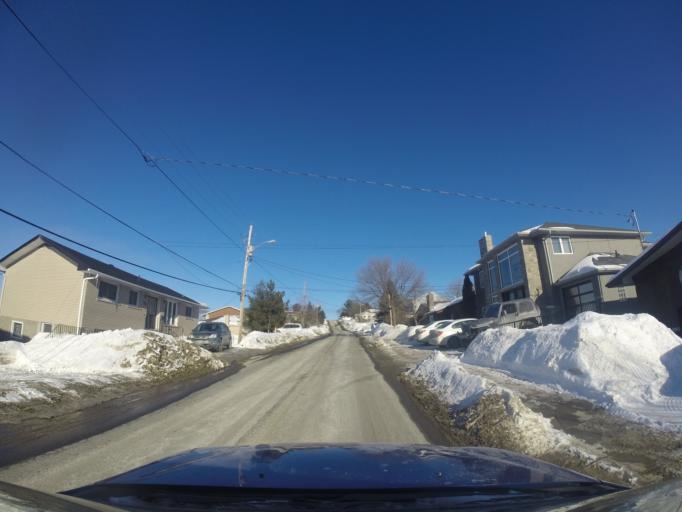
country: CA
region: Ontario
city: Greater Sudbury
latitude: 46.4565
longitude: -80.9971
